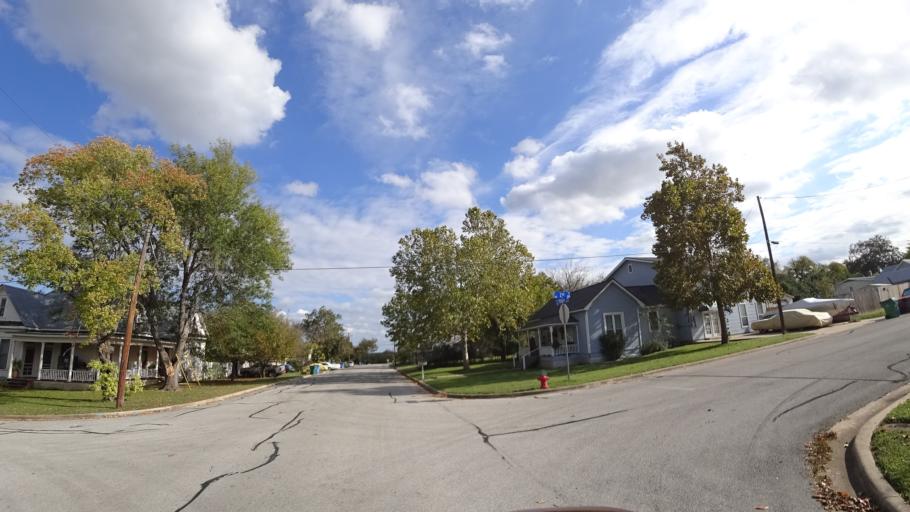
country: US
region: Texas
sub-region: Travis County
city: Pflugerville
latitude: 30.4388
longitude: -97.6229
